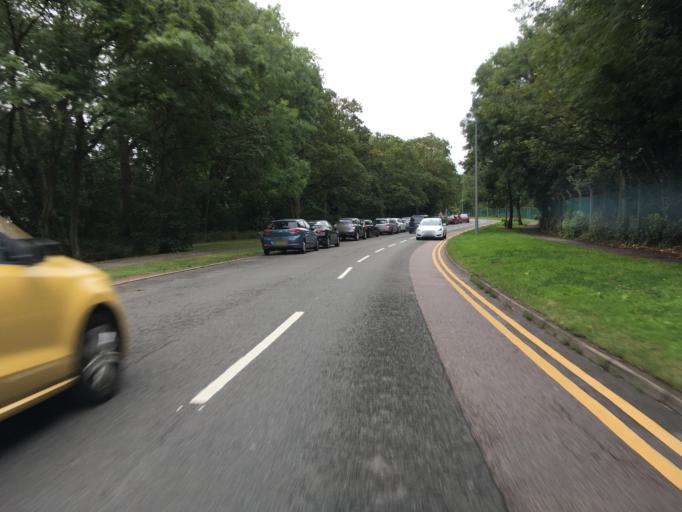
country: GB
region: England
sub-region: Buckinghamshire
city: Bletchley
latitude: 51.9990
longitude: -0.7382
